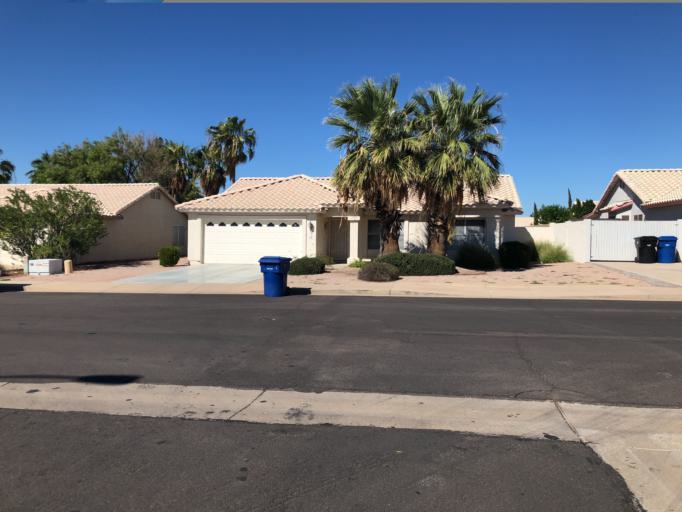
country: US
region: Arizona
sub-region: Maricopa County
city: Mesa
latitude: 33.4714
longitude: -111.6970
